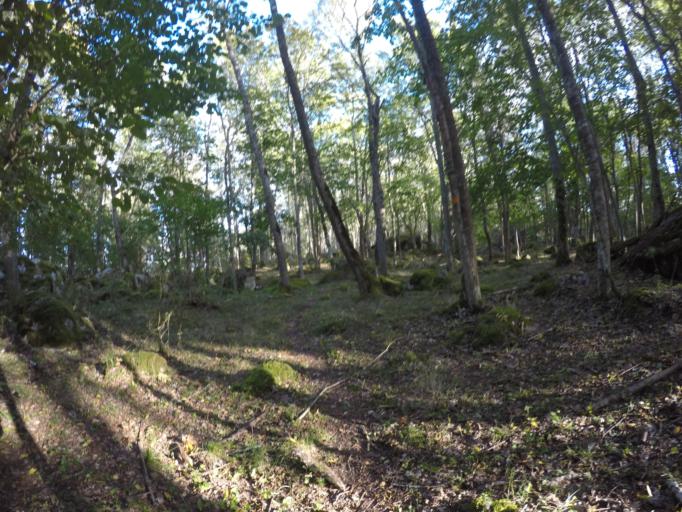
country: SE
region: Soedermanland
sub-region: Eskilstuna Kommun
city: Kvicksund
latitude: 59.4789
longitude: 16.2502
